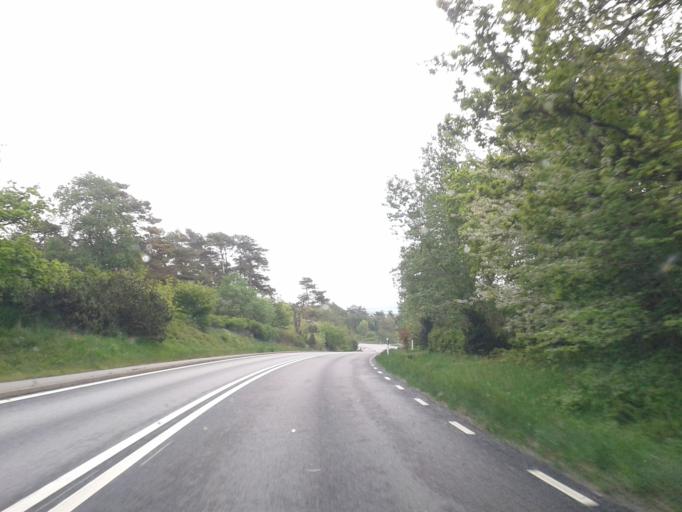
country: SE
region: Vaestra Goetaland
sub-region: Kungalvs Kommun
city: Marstrand
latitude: 57.8940
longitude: 11.6460
